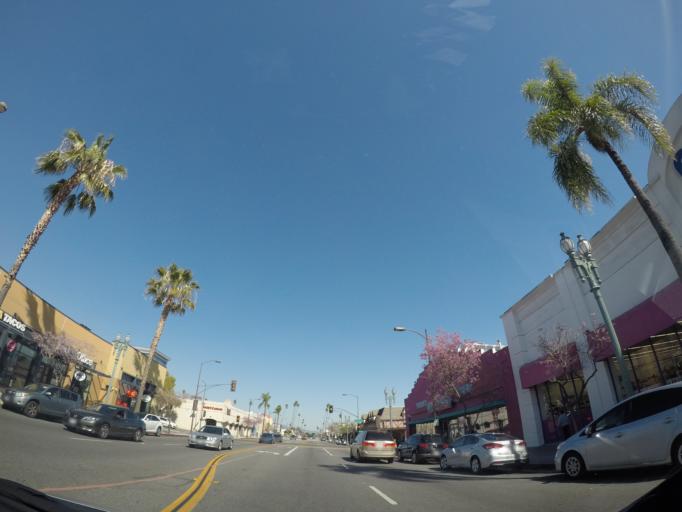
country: US
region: California
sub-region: Los Angeles County
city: East Pasadena
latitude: 34.1460
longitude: -118.1150
